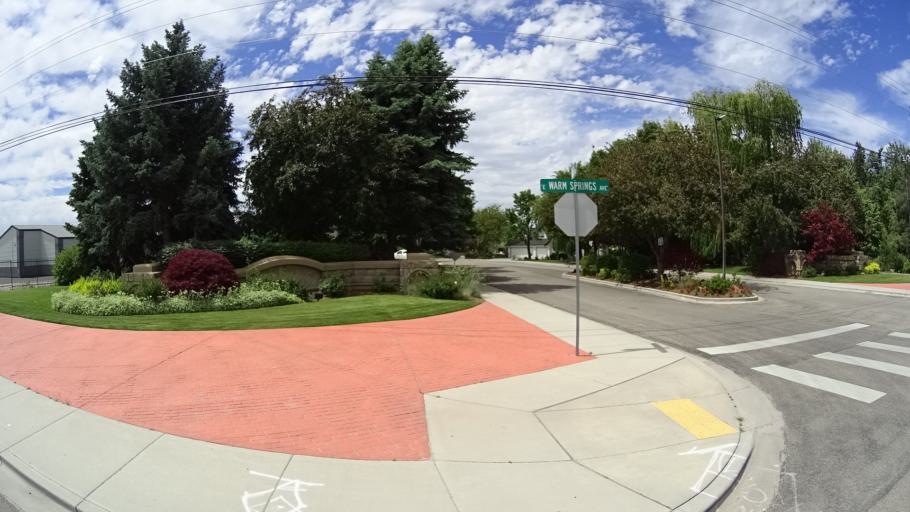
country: US
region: Idaho
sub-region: Ada County
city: Boise
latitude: 43.6008
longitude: -116.1680
